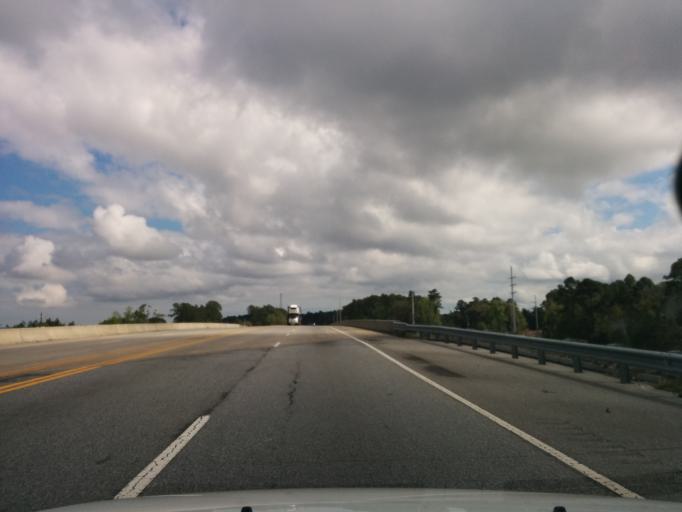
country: US
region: Georgia
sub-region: Glynn County
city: Brunswick
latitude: 31.1214
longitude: -81.5439
